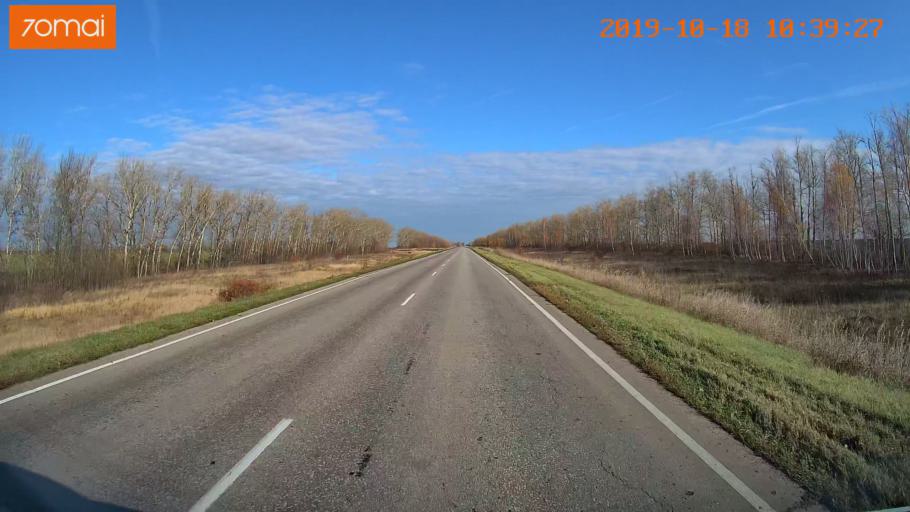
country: RU
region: Tula
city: Kurkino
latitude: 53.5871
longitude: 38.6531
